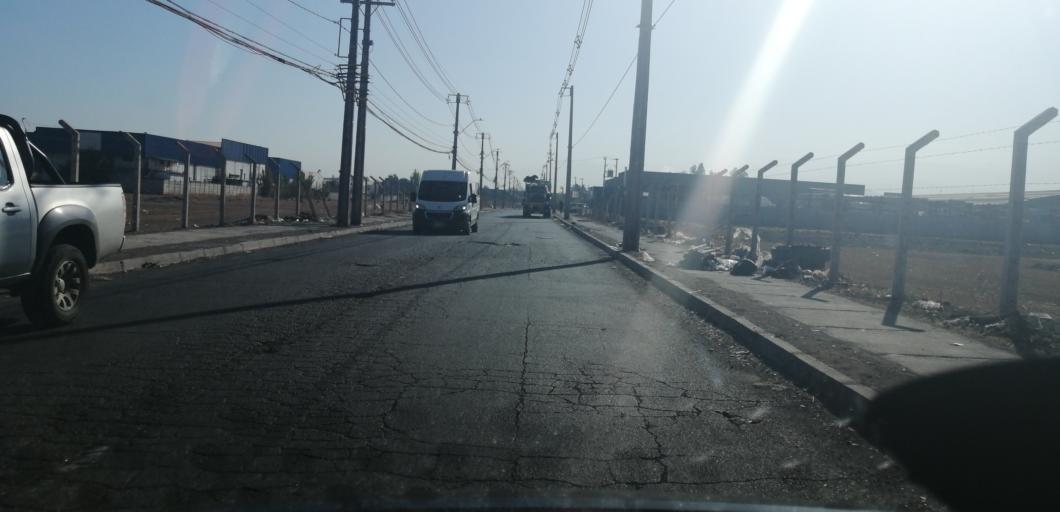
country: CL
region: Santiago Metropolitan
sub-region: Provincia de Santiago
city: Lo Prado
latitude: -33.3816
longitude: -70.7667
